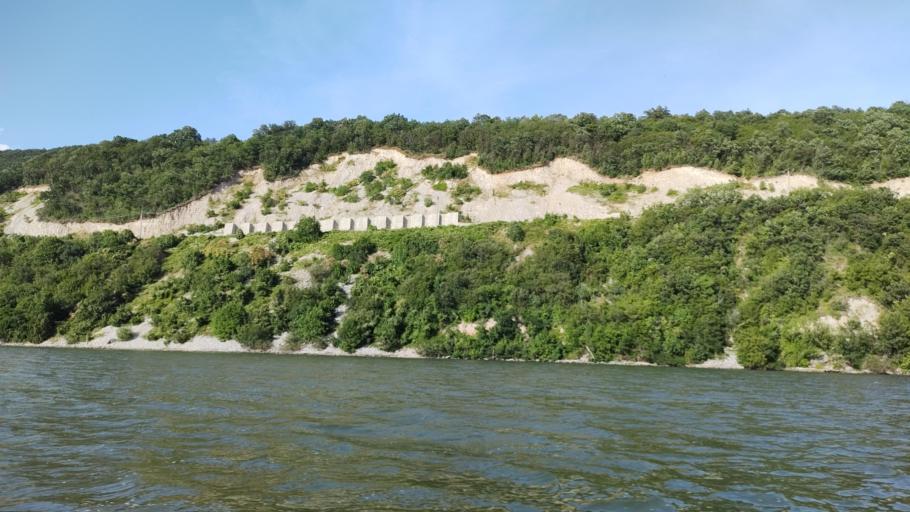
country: RO
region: Mehedinti
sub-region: Comuna Svinita
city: Svinita
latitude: 44.5095
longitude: 22.0800
